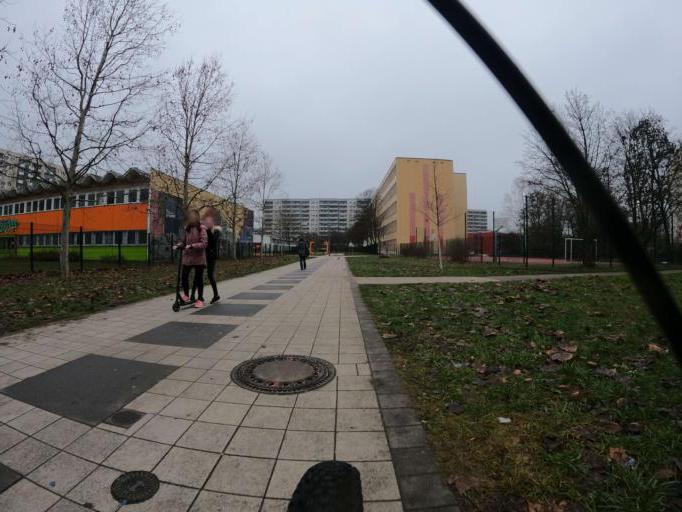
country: DE
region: Berlin
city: Marzahn
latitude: 52.5578
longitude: 13.5613
